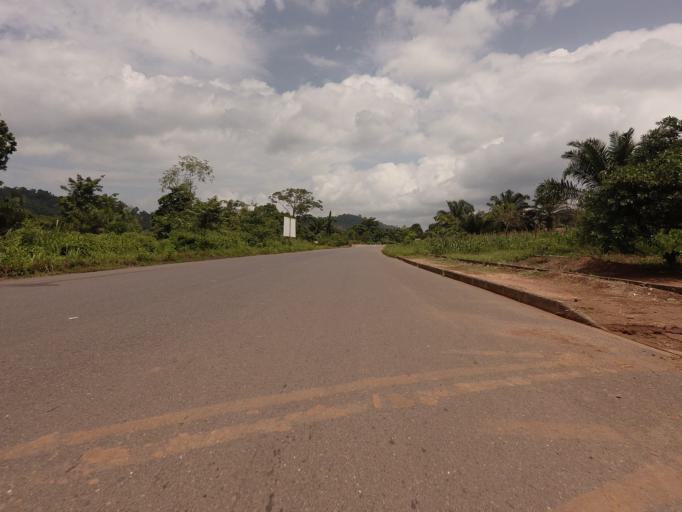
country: GH
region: Volta
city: Ho
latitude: 6.5152
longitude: 0.2187
